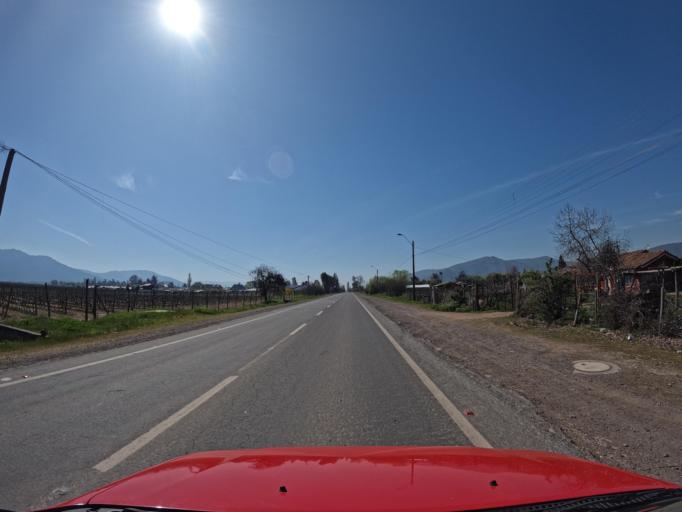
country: CL
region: Maule
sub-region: Provincia de Curico
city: Rauco
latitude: -35.0404
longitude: -71.4546
